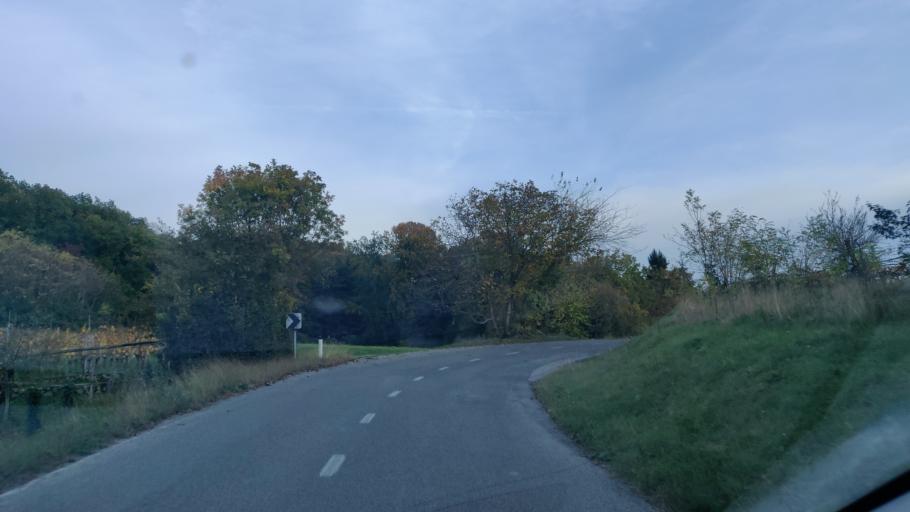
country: SI
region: Sezana
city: Sezana
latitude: 45.7906
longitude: 13.8613
